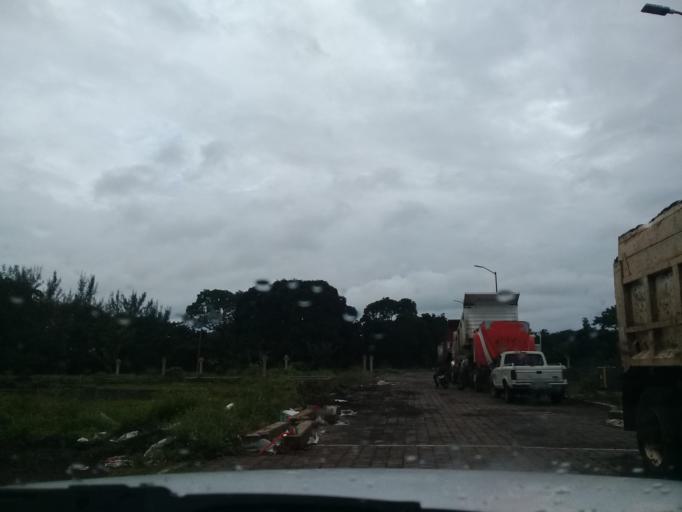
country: MX
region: Veracruz
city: San Andres Tuxtla
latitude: 18.4268
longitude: -95.2173
